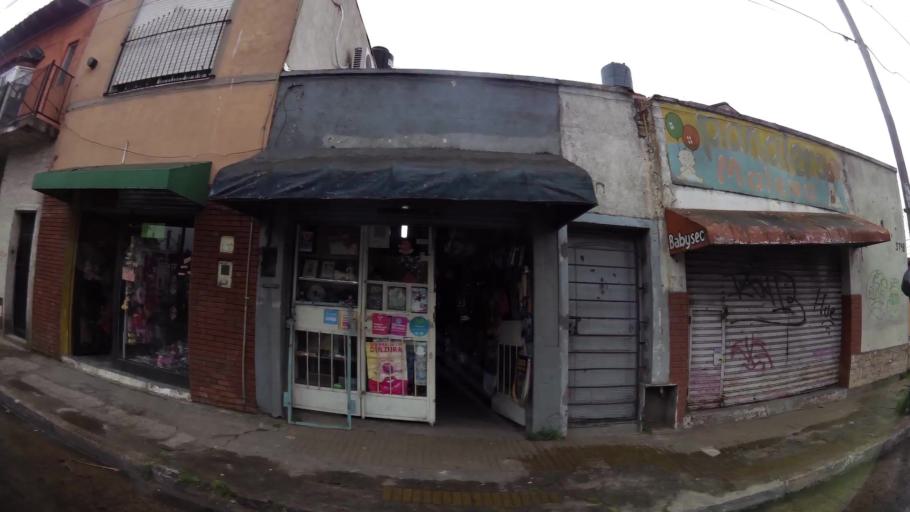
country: AR
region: Buenos Aires
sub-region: Partido de Quilmes
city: Quilmes
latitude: -34.7606
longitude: -58.2253
